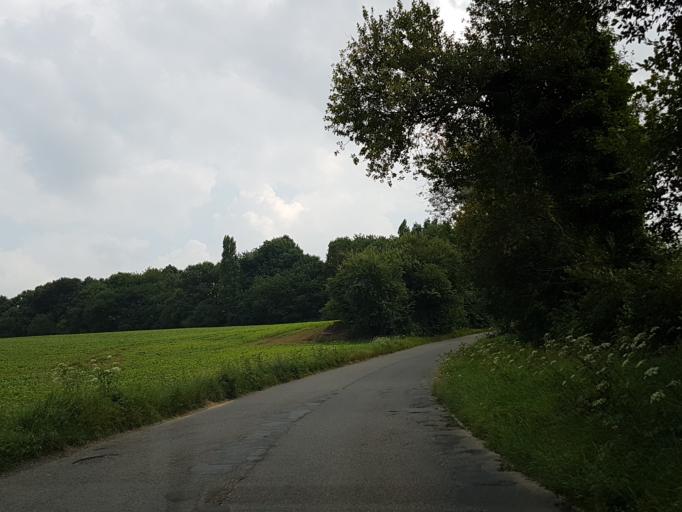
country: BE
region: Flanders
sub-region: Provincie Vlaams-Brabant
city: Kraainem
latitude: 50.8670
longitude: 4.4793
